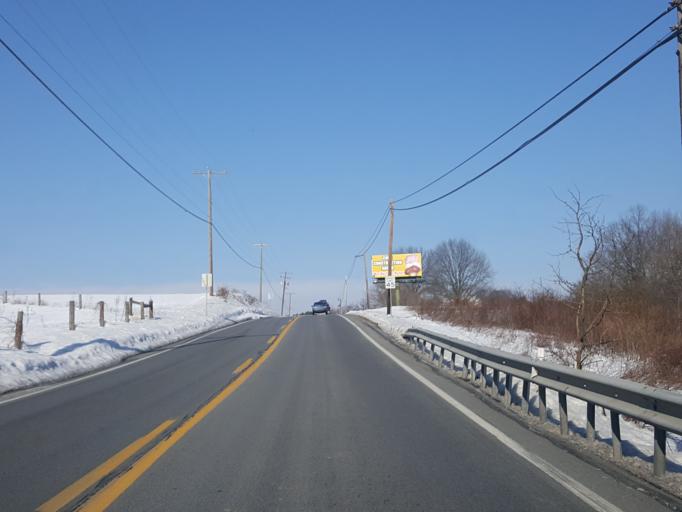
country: US
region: Pennsylvania
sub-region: Berks County
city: Womelsdorf
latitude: 40.4657
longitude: -76.1459
